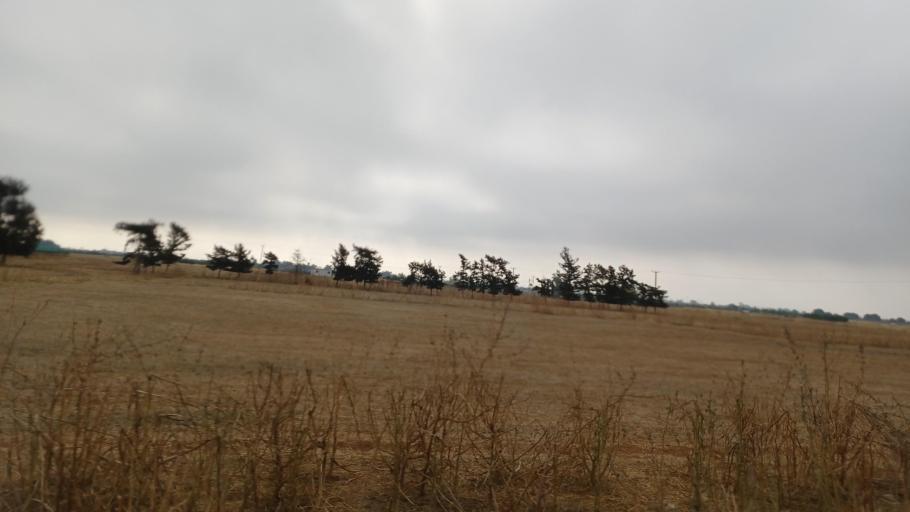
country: CY
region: Ammochostos
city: Achna
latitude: 35.0417
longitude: 33.7909
